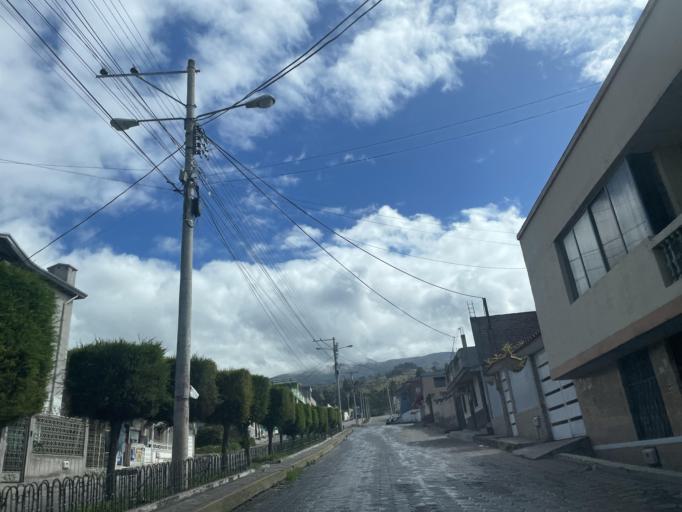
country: EC
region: Chimborazo
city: Guano
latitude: -1.6041
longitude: -78.6427
